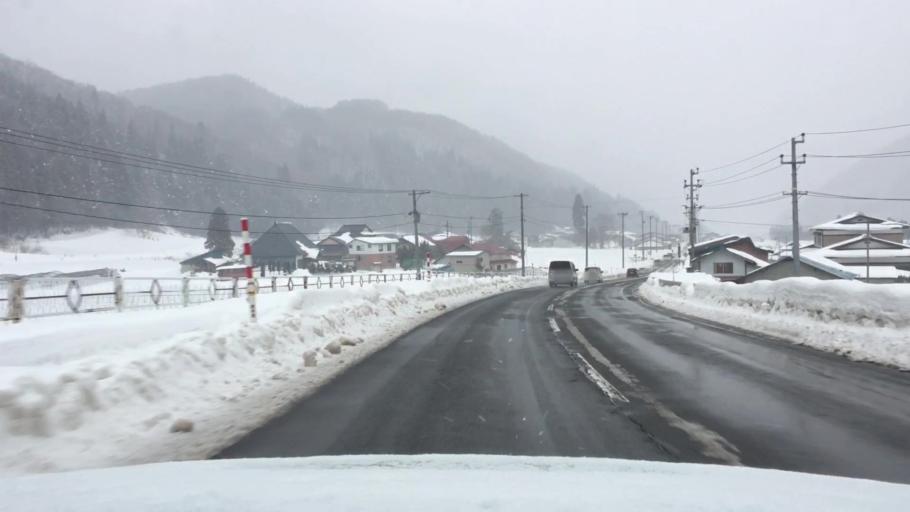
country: JP
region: Akita
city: Hanawa
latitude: 40.0651
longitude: 141.0154
